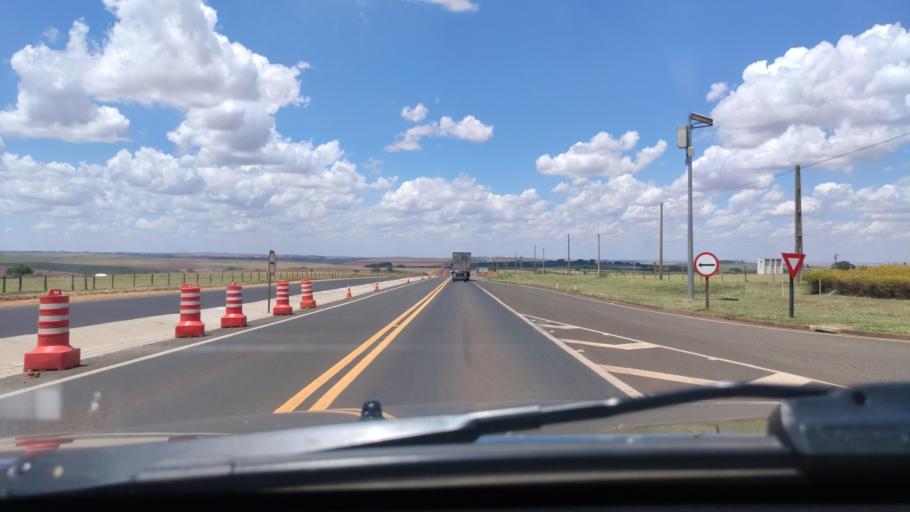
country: BR
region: Sao Paulo
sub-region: Jau
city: Jau
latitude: -22.1952
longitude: -48.5075
